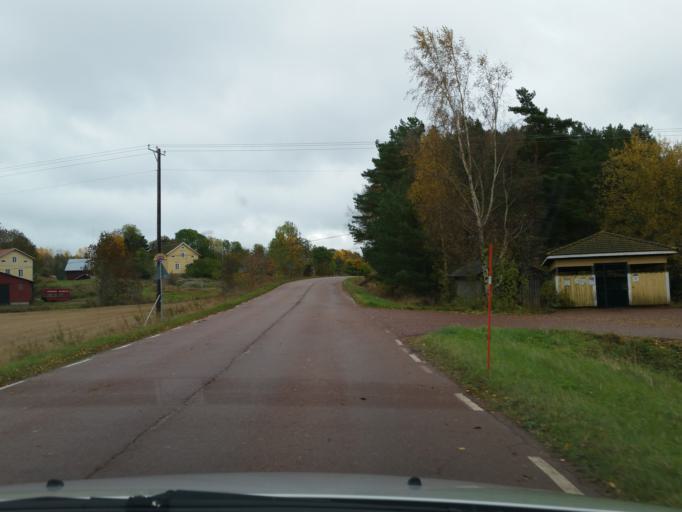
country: AX
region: Alands landsbygd
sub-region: Lumparland
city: Lumparland
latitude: 60.1165
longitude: 20.2592
